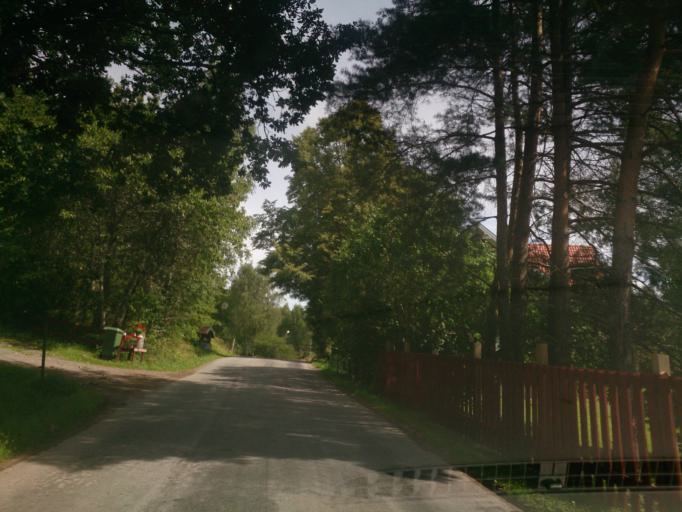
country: SE
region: OEstergoetland
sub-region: Valdemarsviks Kommun
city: Gusum
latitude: 58.2842
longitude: 16.5248
